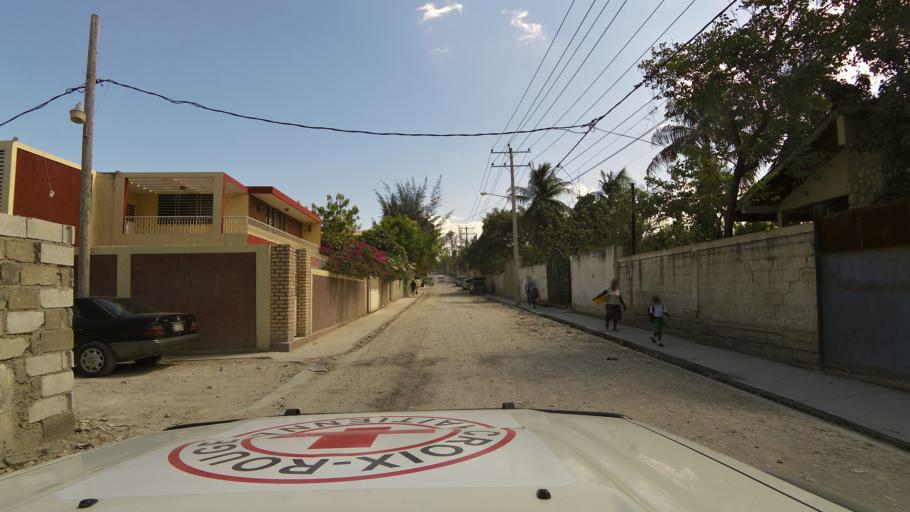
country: HT
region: Ouest
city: Delmas 73
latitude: 18.5613
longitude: -72.3003
